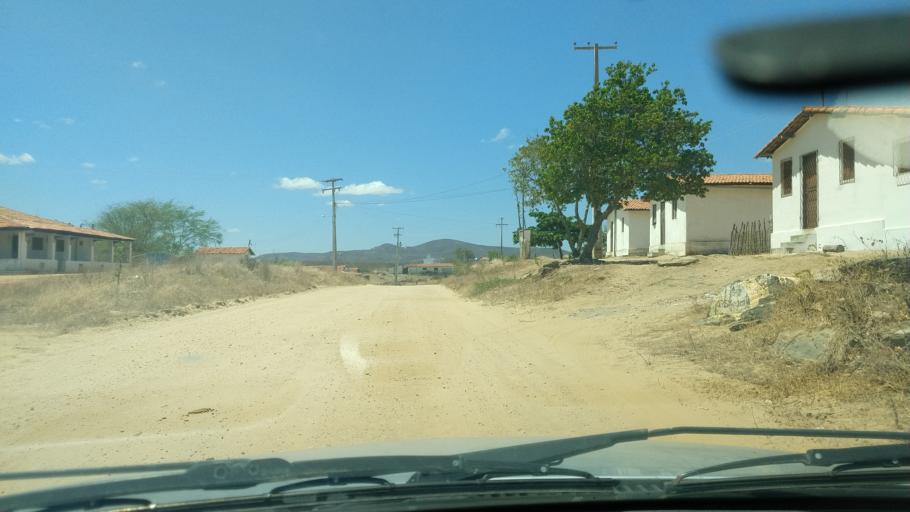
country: BR
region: Rio Grande do Norte
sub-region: Sao Tome
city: Sao Tome
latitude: -5.9795
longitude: -36.1741
